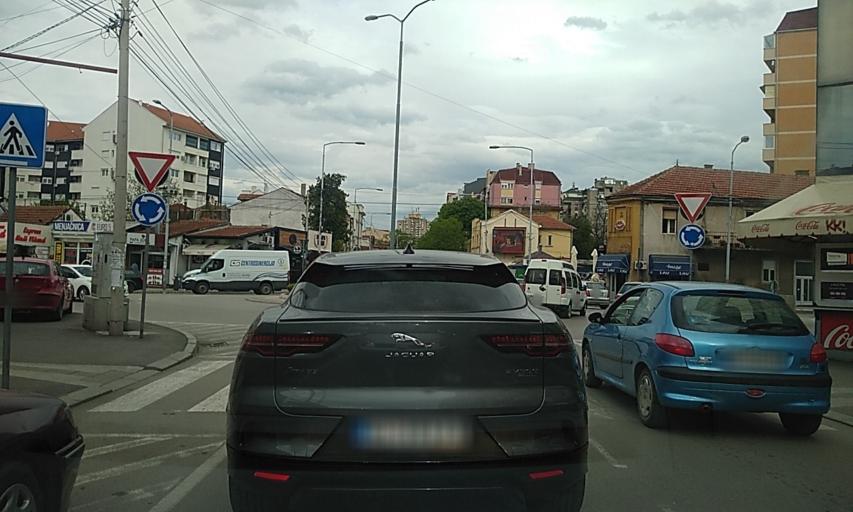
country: RS
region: Central Serbia
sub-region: Nisavski Okrug
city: Nis
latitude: 43.3175
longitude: 21.8994
